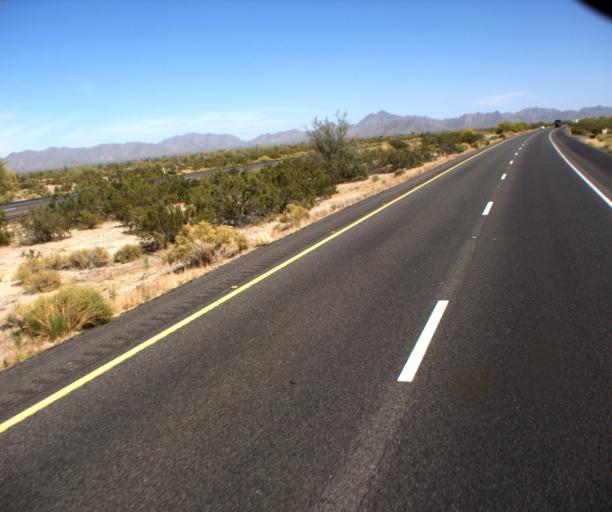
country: US
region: Arizona
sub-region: Maricopa County
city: Gila Bend
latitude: 32.9067
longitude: -112.5355
